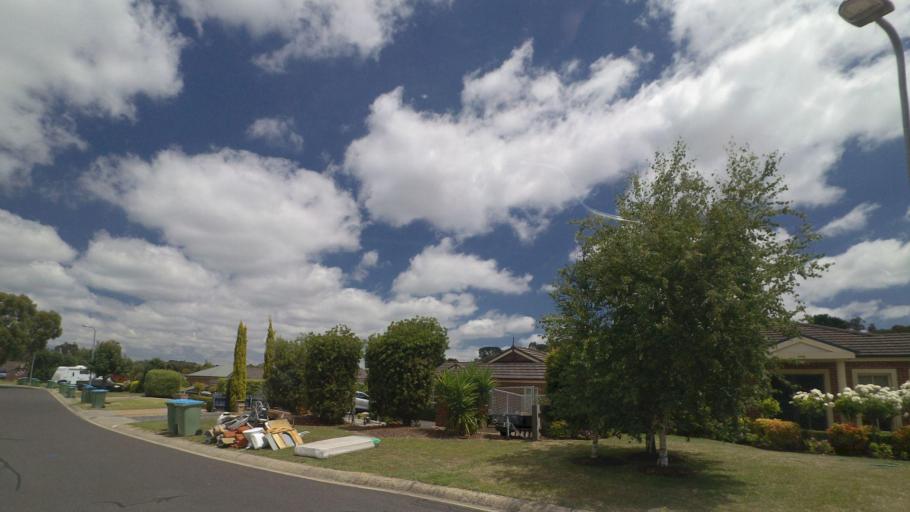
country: AU
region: Victoria
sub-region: Maroondah
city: Croydon Hills
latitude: -37.7666
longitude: 145.2691
